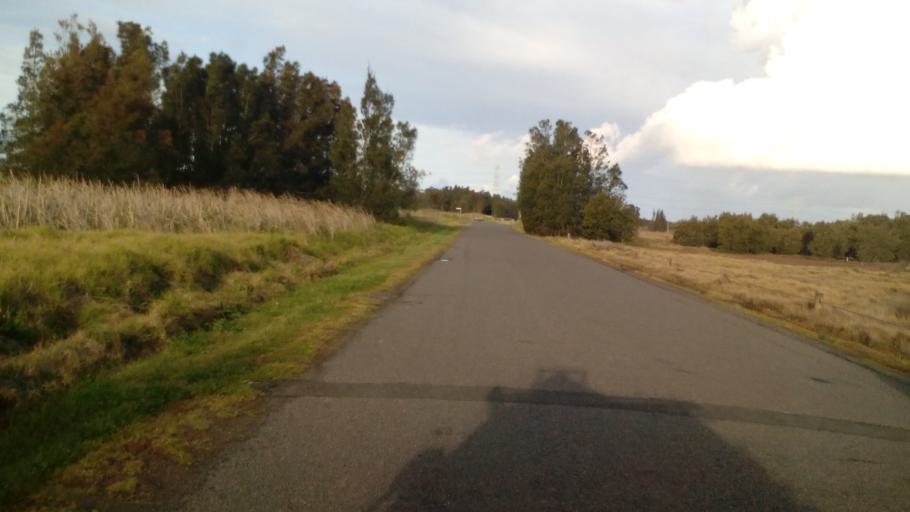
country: AU
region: New South Wales
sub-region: Newcastle
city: Mayfield West
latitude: -32.8451
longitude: 151.7006
